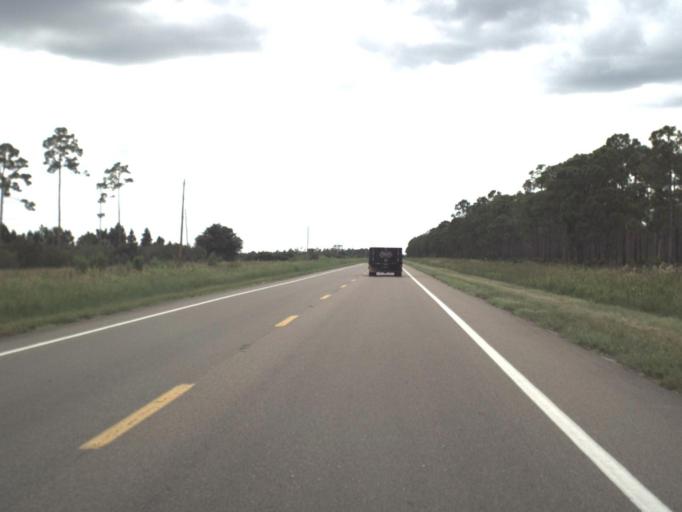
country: US
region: Florida
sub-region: Lee County
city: Olga
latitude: 26.8676
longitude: -81.7598
